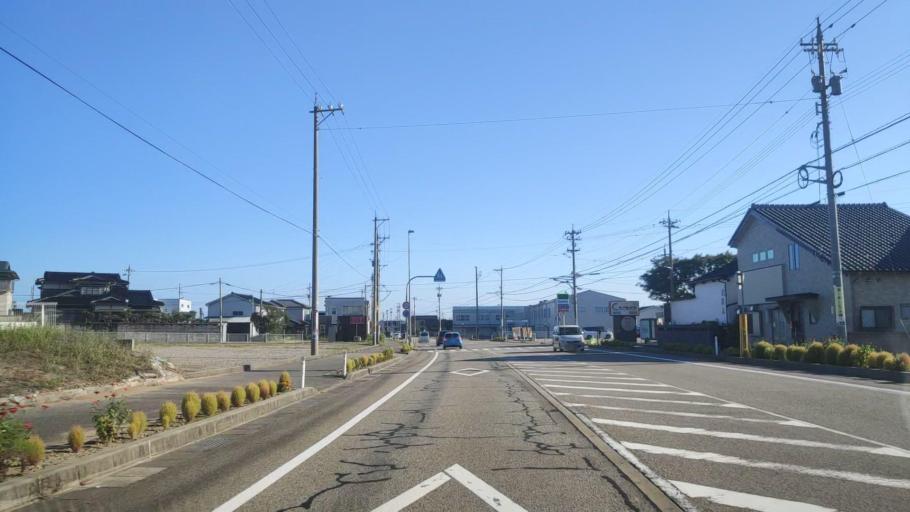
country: JP
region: Ishikawa
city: Tsubata
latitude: 36.7432
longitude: 136.7079
